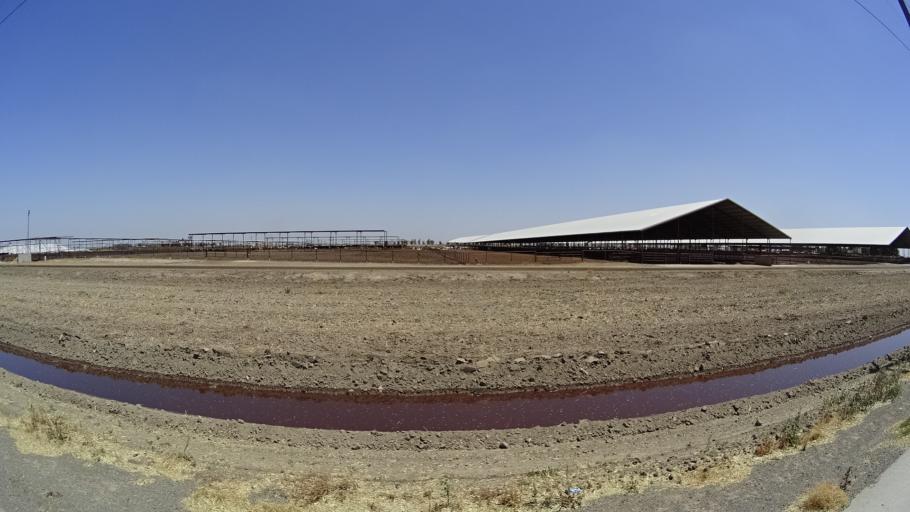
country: US
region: California
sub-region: Kings County
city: Home Garden
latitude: 36.1996
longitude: -119.6459
